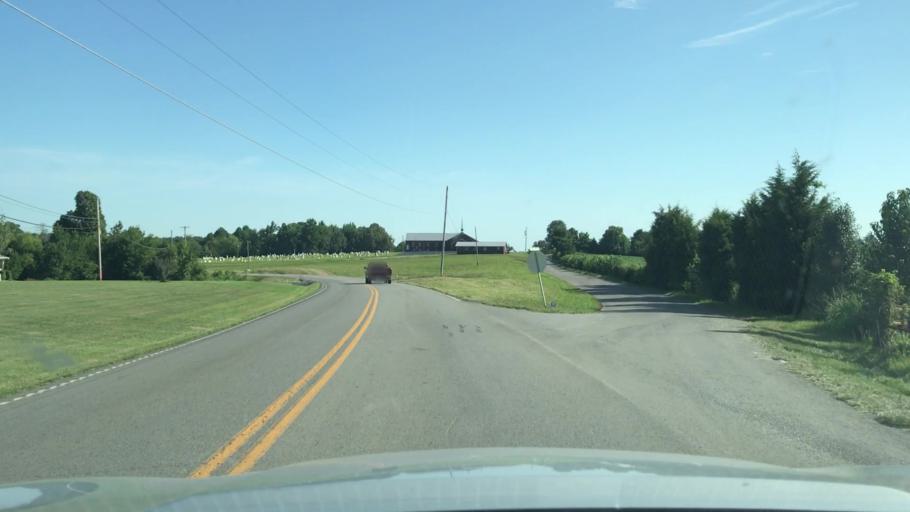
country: US
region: Kentucky
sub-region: Muhlenberg County
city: Greenville
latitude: 37.1772
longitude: -87.1525
